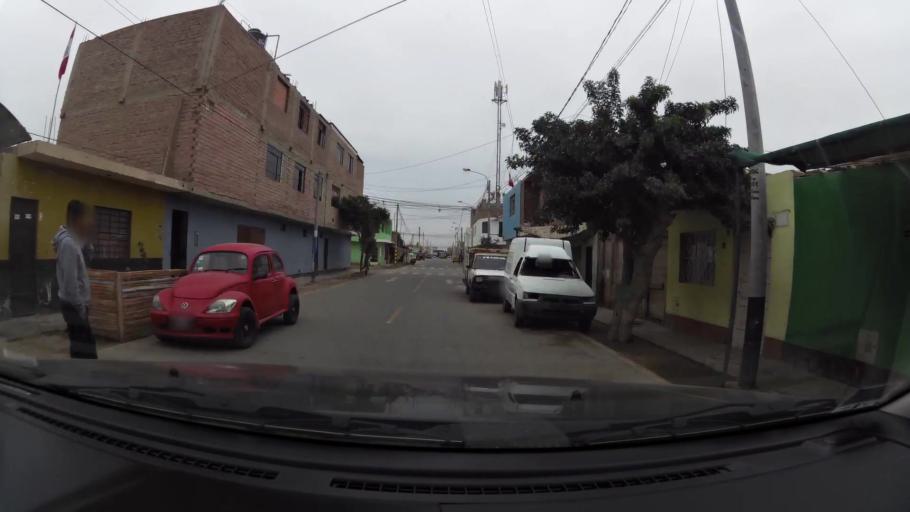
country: PE
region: Ica
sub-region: Provincia de Pisco
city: Pisco
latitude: -13.7148
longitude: -76.1984
